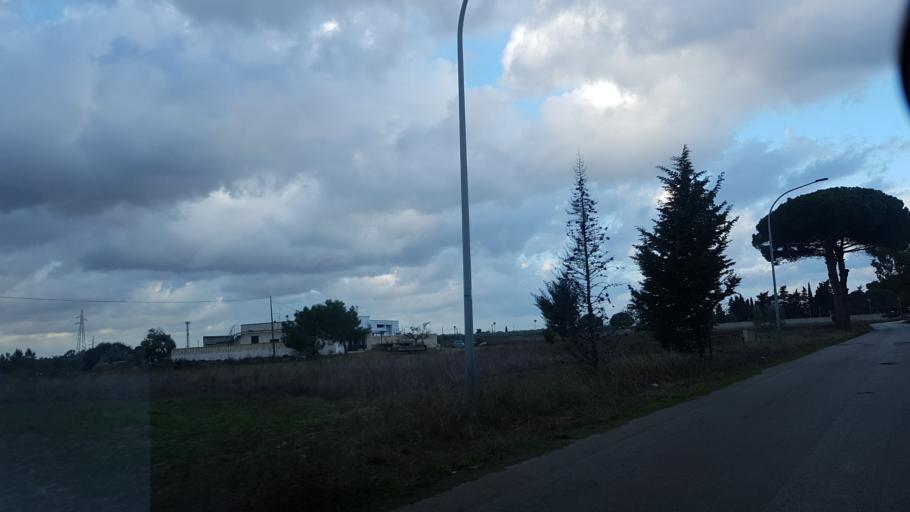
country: IT
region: Apulia
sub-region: Provincia di Brindisi
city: San Pietro Vernotico
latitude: 40.4965
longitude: 18.0025
